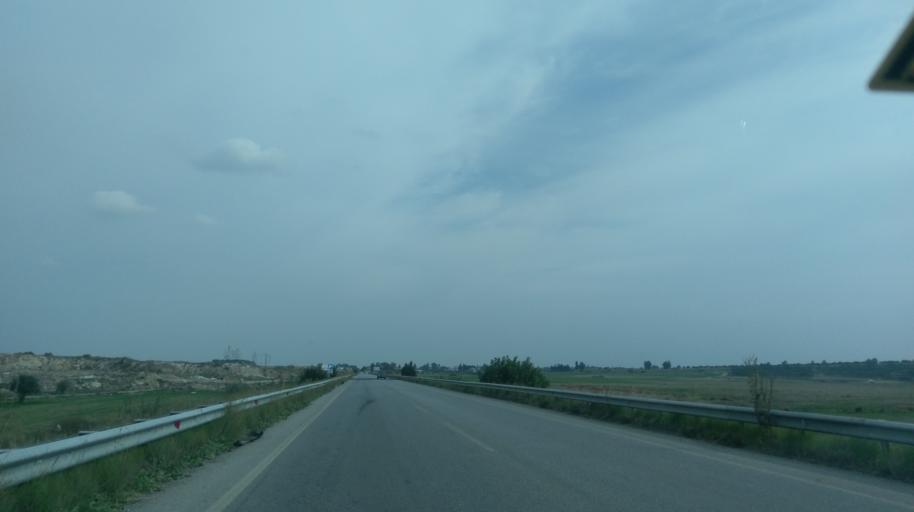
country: CY
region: Ammochostos
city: Lefkonoiko
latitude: 35.2611
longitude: 33.7645
